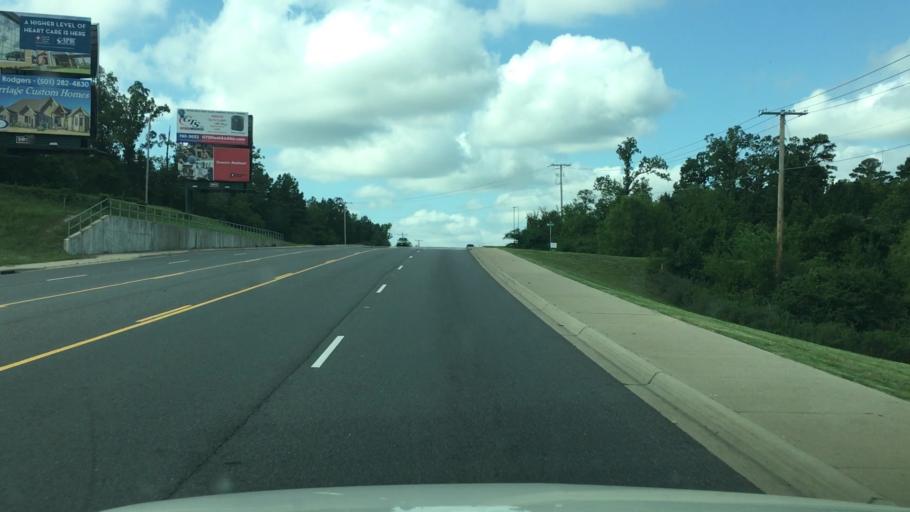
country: US
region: Arkansas
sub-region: Garland County
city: Lake Hamilton
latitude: 34.4629
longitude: -93.0746
